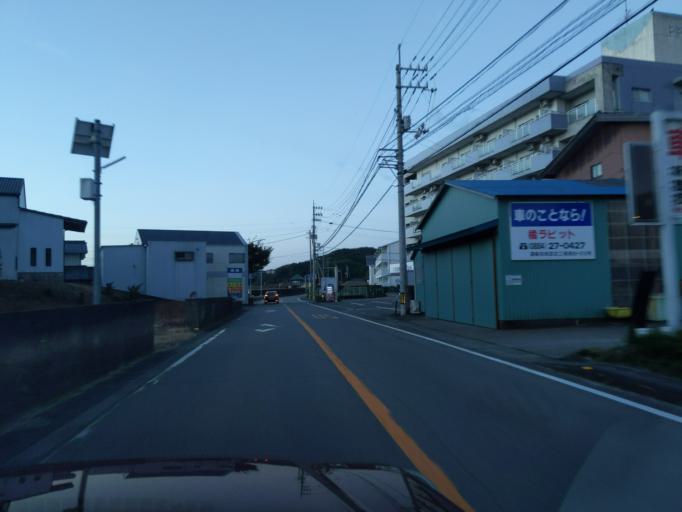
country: JP
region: Tokushima
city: Anan
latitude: 33.8638
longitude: 134.6318
